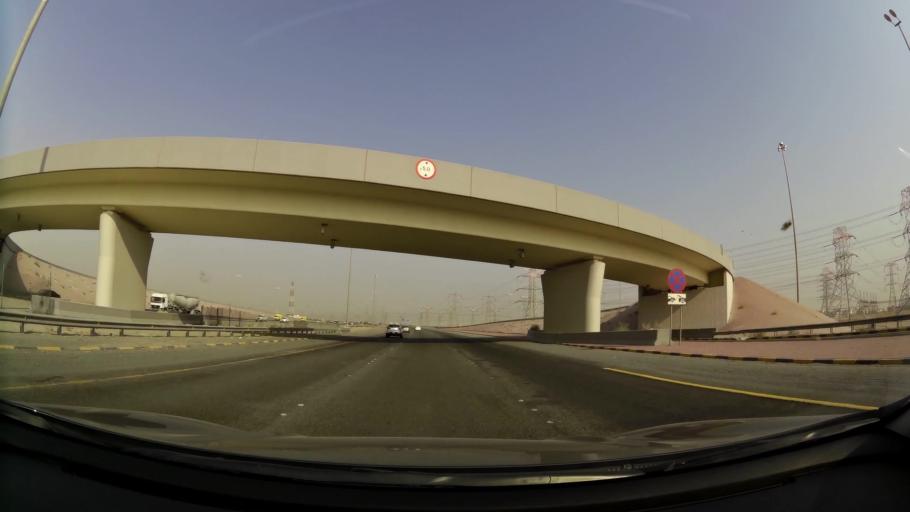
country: KW
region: Al Asimah
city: Ar Rabiyah
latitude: 29.2347
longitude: 47.8836
